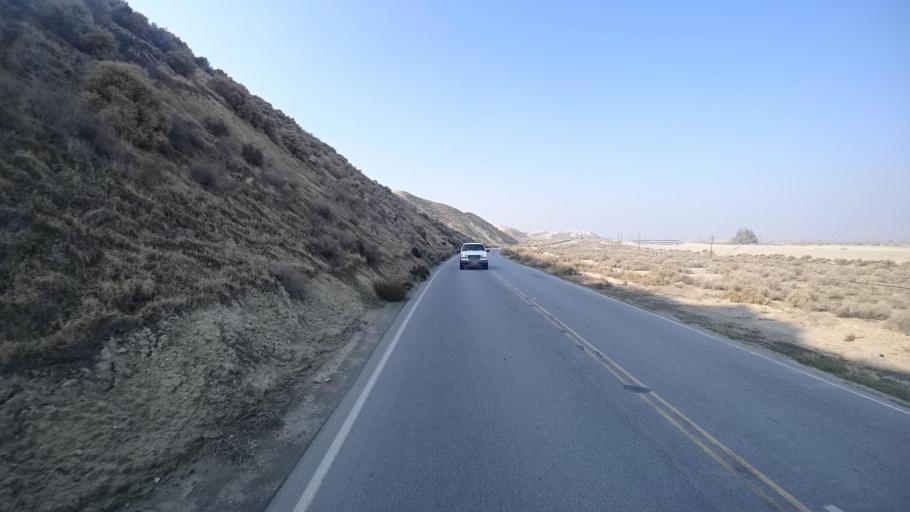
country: US
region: California
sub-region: Kern County
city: Ford City
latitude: 35.2720
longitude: -119.3173
